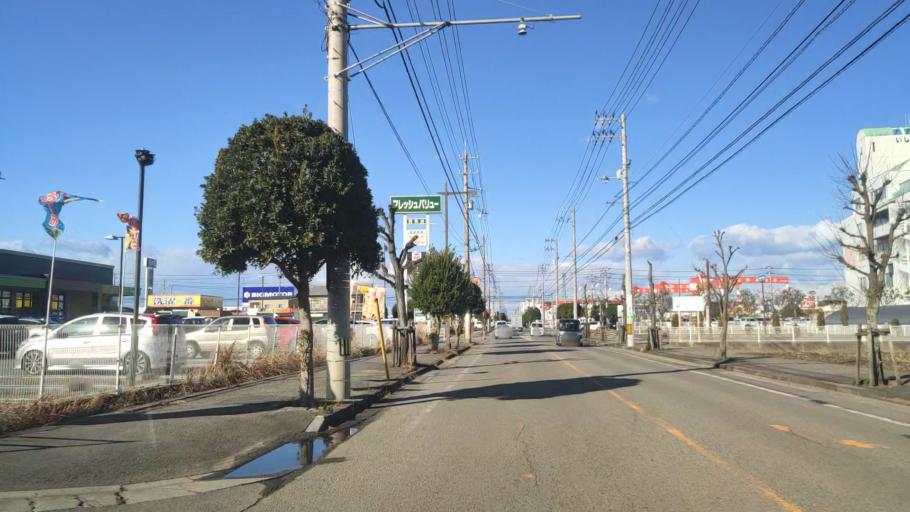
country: JP
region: Ehime
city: Saijo
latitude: 33.9279
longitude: 133.1905
